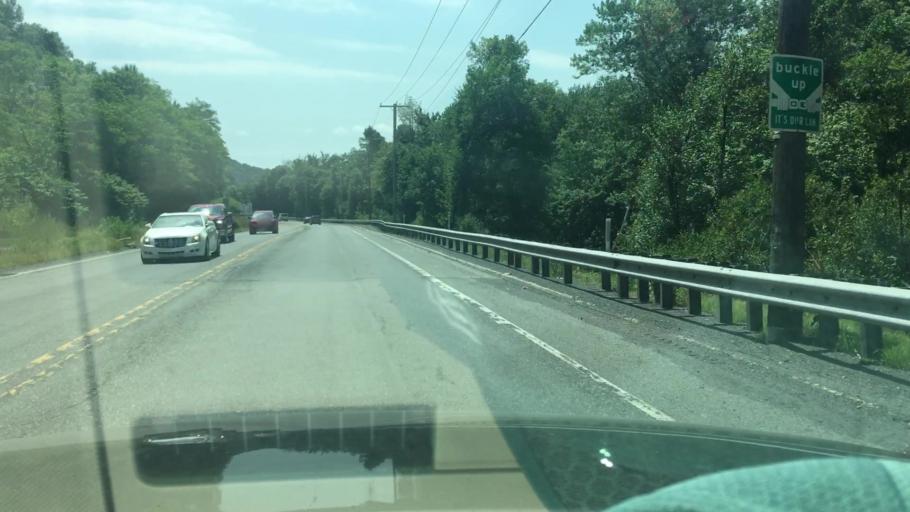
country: US
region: Pennsylvania
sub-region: Schuylkill County
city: Tamaqua
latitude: 40.7916
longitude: -75.9667
